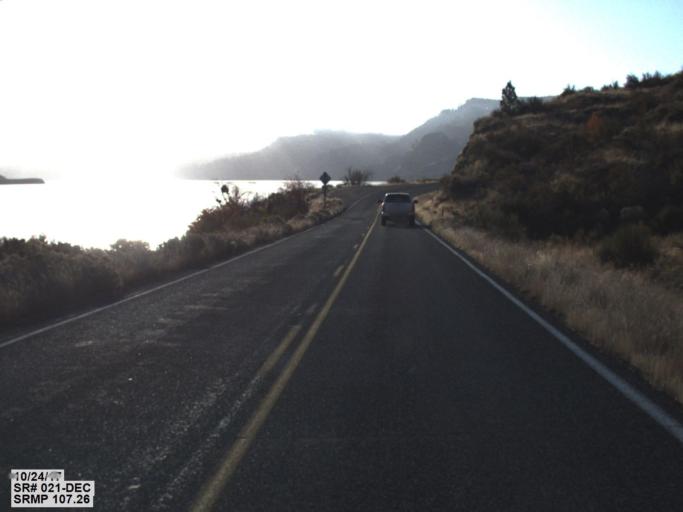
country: US
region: Washington
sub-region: Okanogan County
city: Coulee Dam
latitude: 47.9549
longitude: -118.6931
